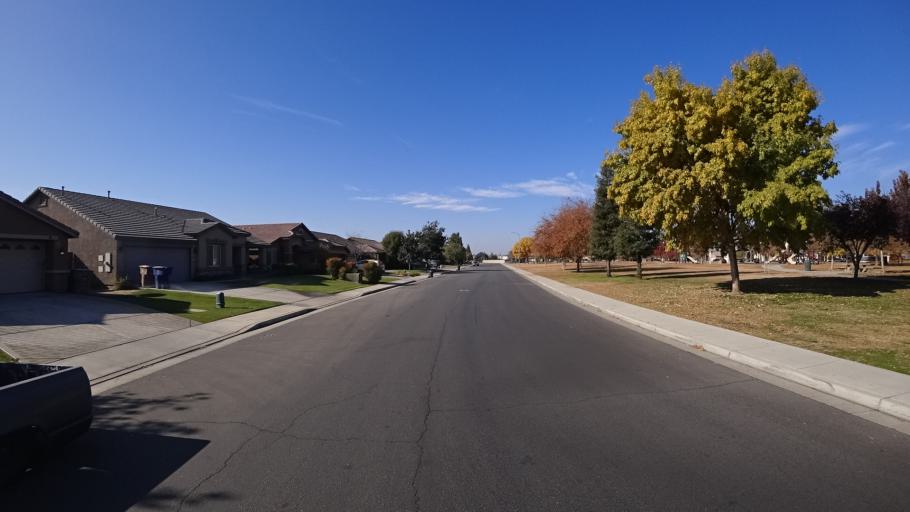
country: US
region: California
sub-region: Kern County
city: Greenfield
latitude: 35.2703
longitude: -119.0576
